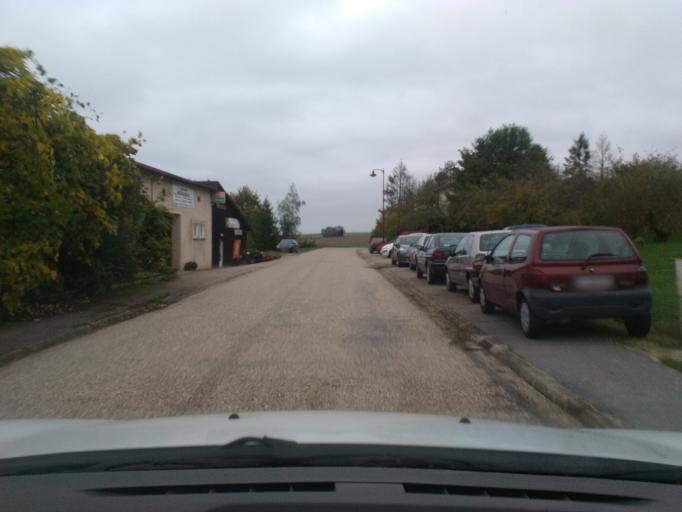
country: FR
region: Lorraine
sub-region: Departement des Vosges
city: Dogneville
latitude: 48.2693
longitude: 6.4921
